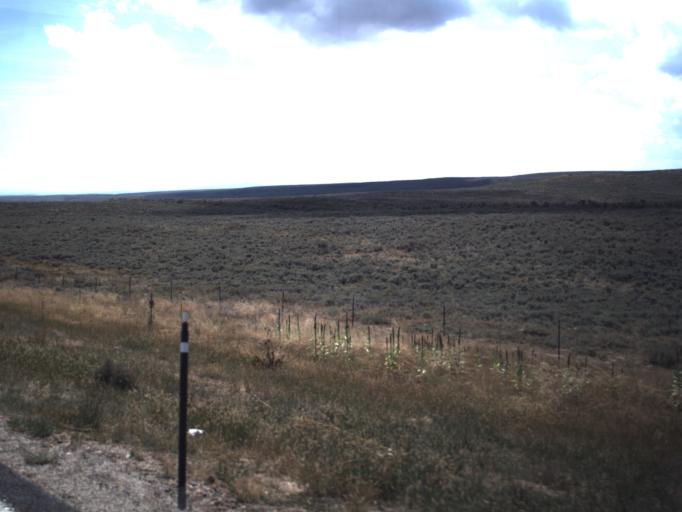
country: US
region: Utah
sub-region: Rich County
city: Randolph
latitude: 41.8032
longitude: -111.2460
